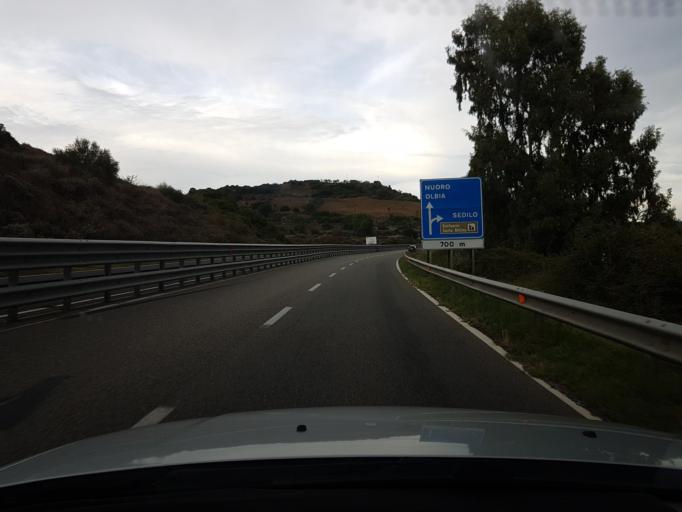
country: IT
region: Sardinia
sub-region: Provincia di Oristano
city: Sedilo
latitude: 40.1629
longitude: 8.9177
